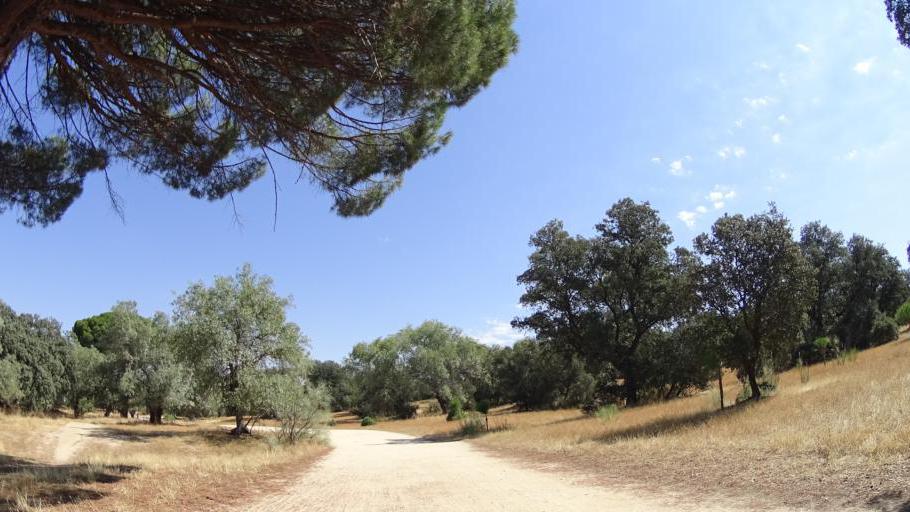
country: ES
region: Madrid
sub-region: Provincia de Madrid
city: Boadilla del Monte
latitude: 40.4157
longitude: -3.8591
